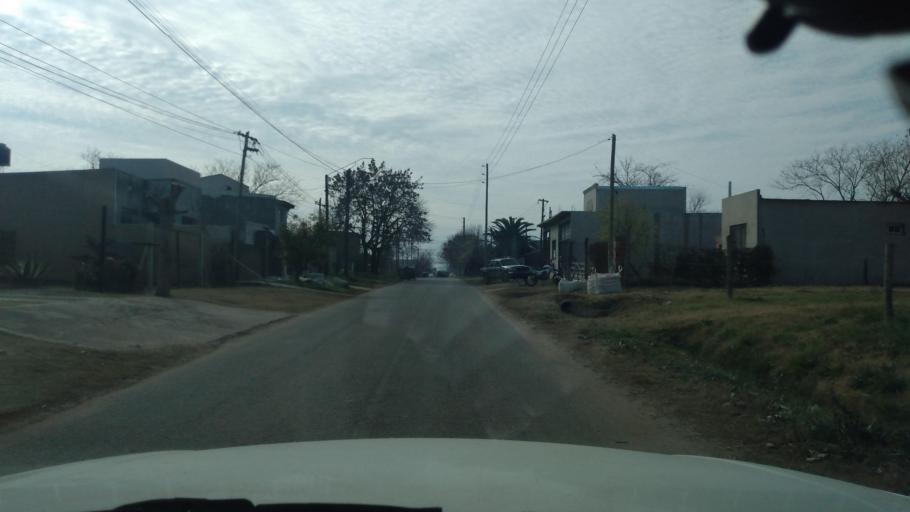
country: AR
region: Buenos Aires
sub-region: Partido de Lujan
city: Lujan
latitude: -34.5814
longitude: -59.1279
